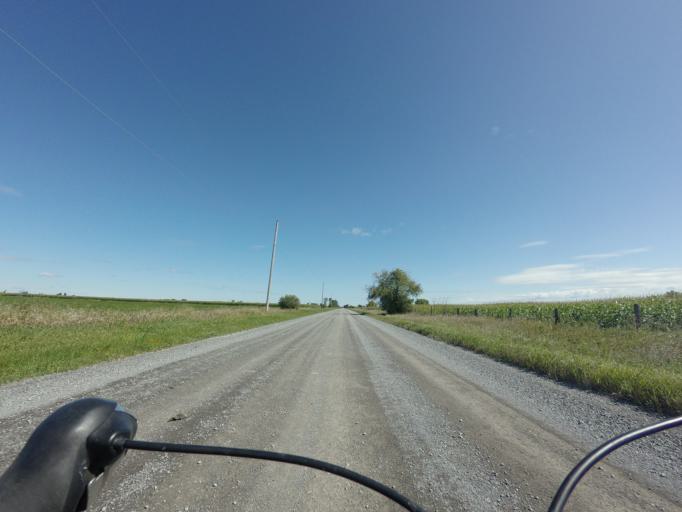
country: CA
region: Ontario
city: Bells Corners
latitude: 45.2214
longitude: -75.8464
